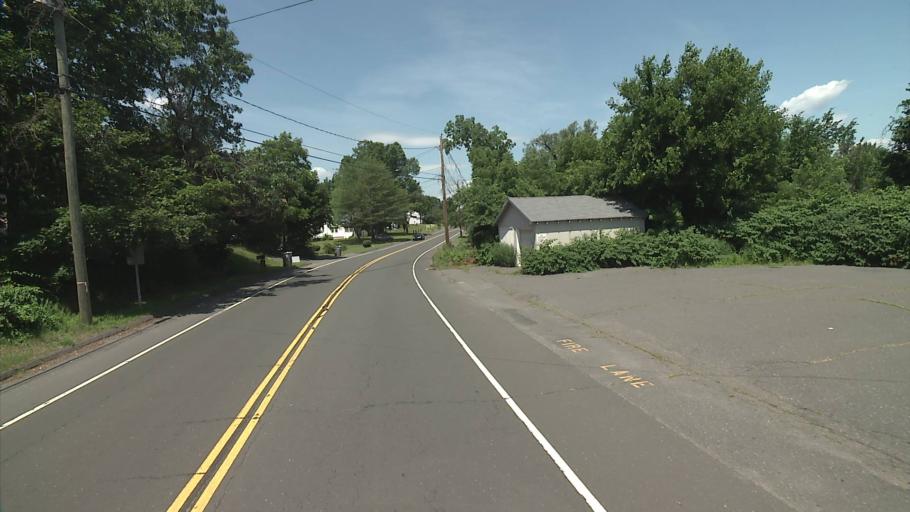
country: US
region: Connecticut
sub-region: Hartford County
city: Plainville
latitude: 41.6705
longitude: -72.8817
